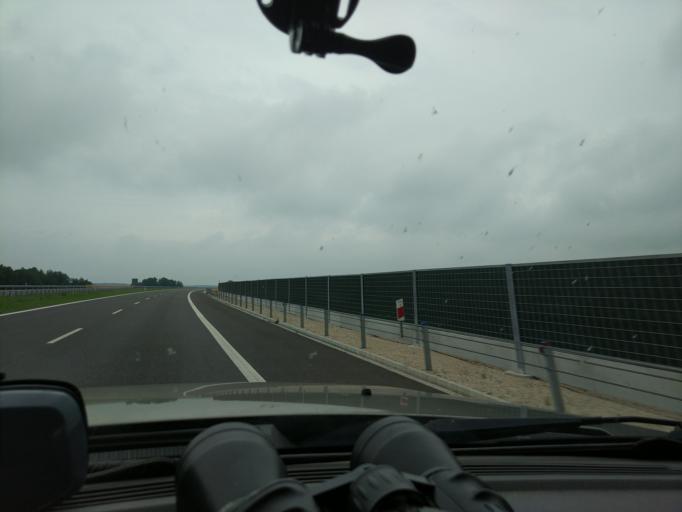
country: PL
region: Podlasie
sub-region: Powiat zambrowski
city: Szumowo
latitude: 52.9420
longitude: 22.1497
